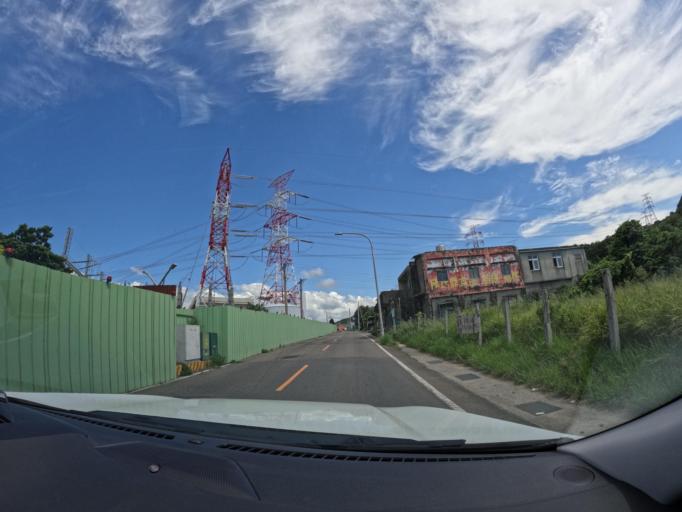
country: TW
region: Taiwan
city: Taoyuan City
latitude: 25.1194
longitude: 121.2968
